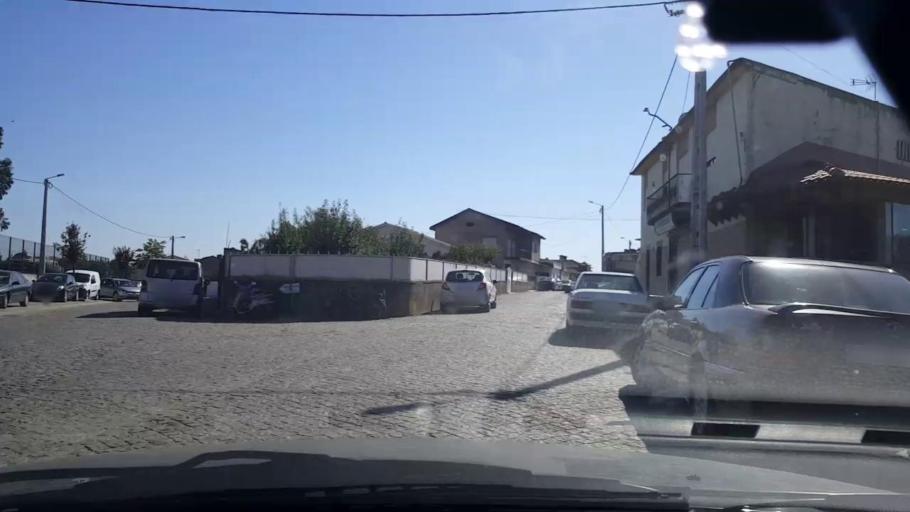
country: PT
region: Braga
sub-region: Vila Nova de Famalicao
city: Ribeirao
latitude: 41.3582
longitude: -8.6264
